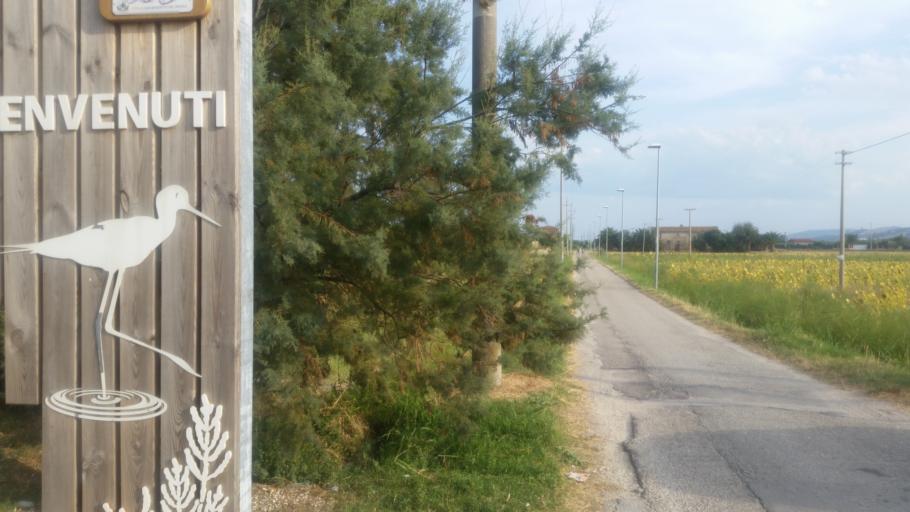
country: IT
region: The Marches
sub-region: Provincia di Ascoli Piceno
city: San Benedetto del Tronto
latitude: 42.9084
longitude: 13.9014
